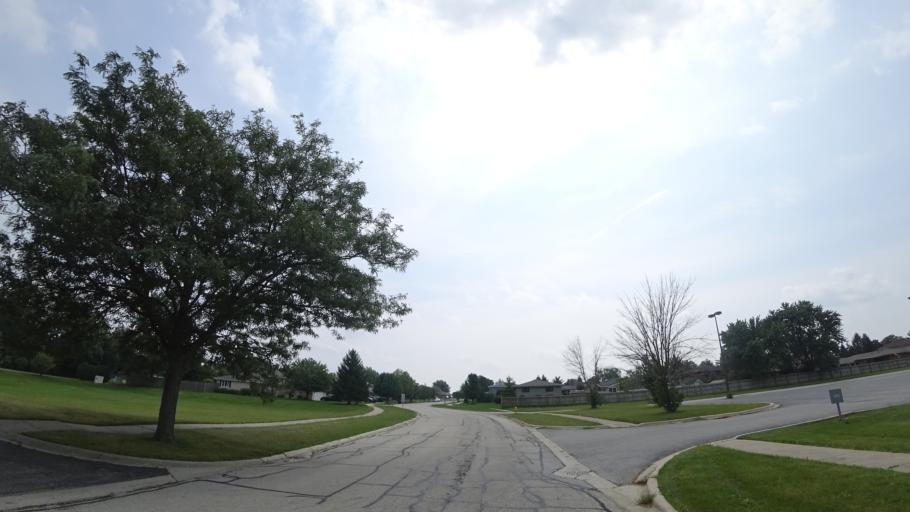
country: US
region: Illinois
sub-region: Will County
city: Goodings Grove
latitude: 41.6289
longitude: -87.9077
